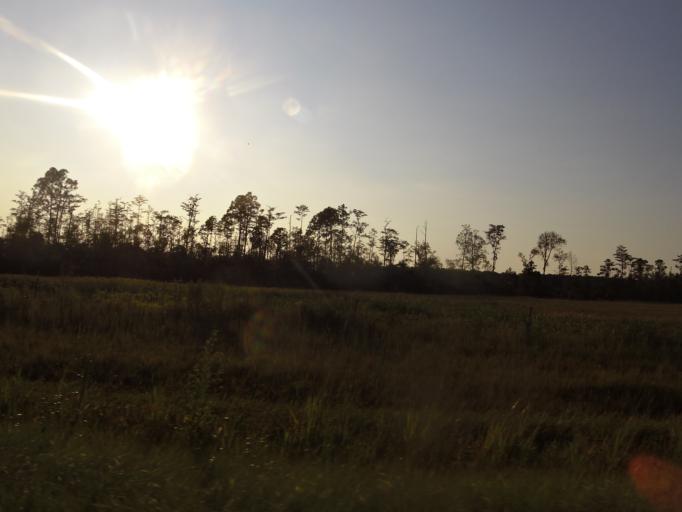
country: US
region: Florida
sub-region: Nassau County
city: Callahan
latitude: 30.5313
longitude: -81.9901
